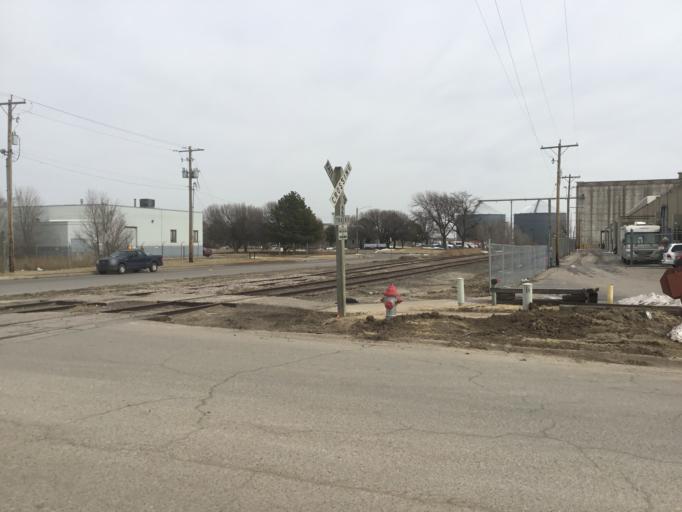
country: US
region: Kansas
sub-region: Sedgwick County
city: Wichita
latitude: 37.7400
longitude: -97.3310
